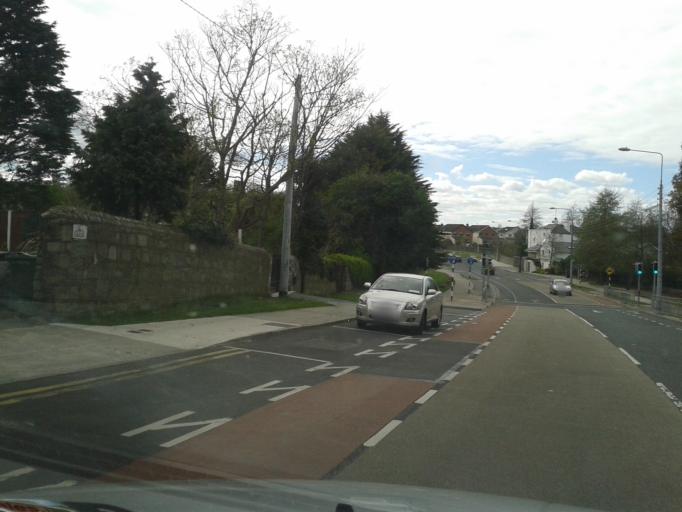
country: IE
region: Leinster
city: Monkstown
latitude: 53.2893
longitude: -6.1479
